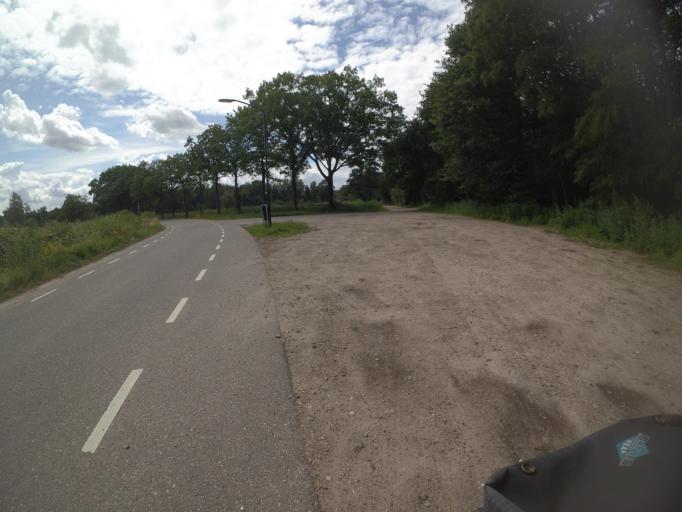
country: NL
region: North Brabant
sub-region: Gemeente Haaren
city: Haaren
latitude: 51.5890
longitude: 5.2435
